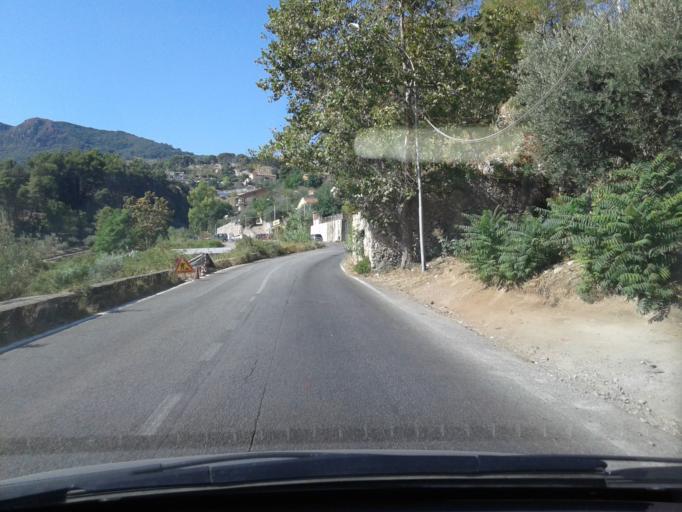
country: IT
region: Sicily
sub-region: Palermo
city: Pioppo
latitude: 38.0419
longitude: 13.2189
